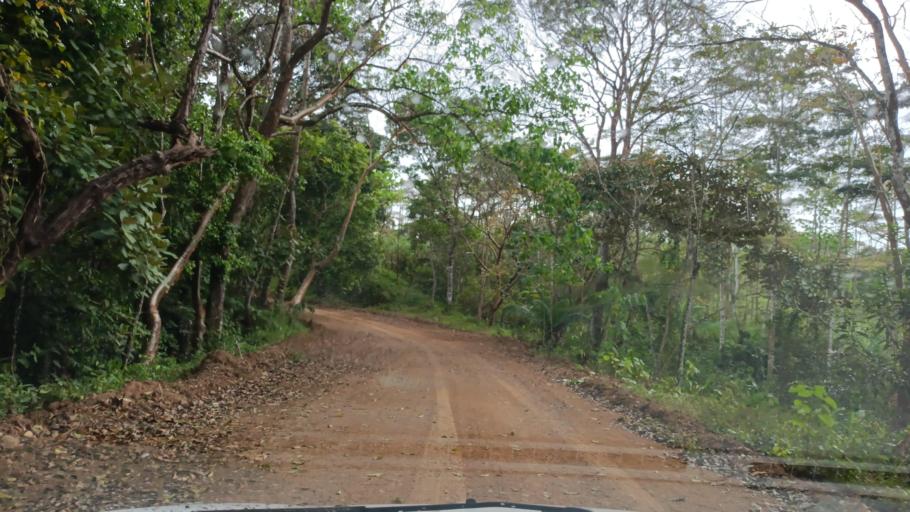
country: PA
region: Panama
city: La Cabima
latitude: 9.1265
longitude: -79.5102
